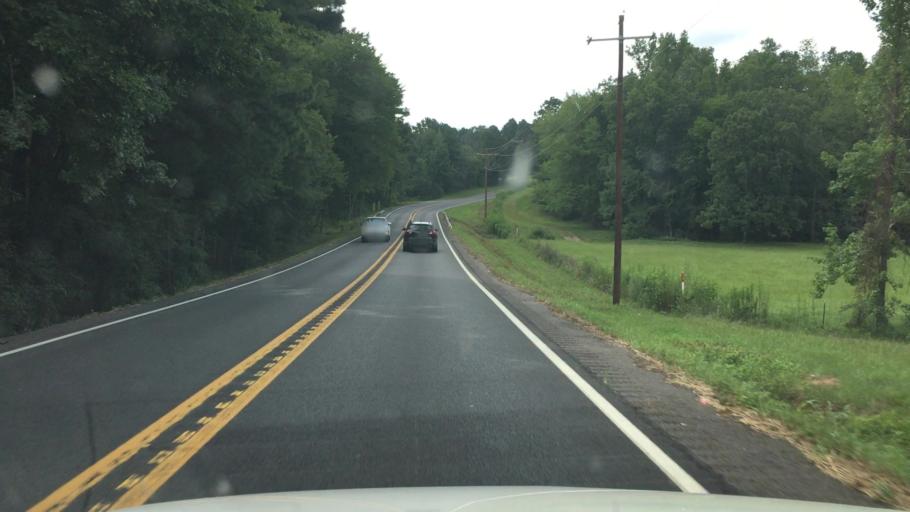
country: US
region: Arkansas
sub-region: Garland County
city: Lake Hamilton
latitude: 34.3313
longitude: -93.1755
